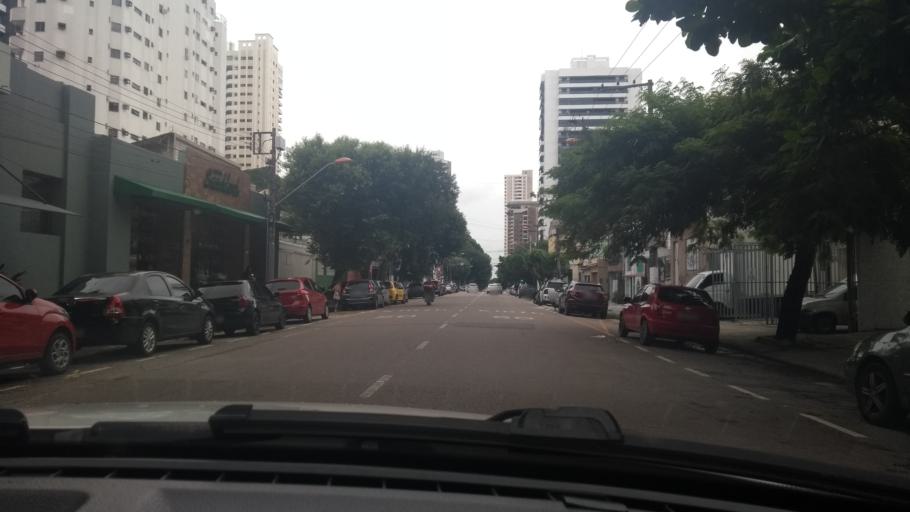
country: BR
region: Para
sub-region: Belem
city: Belem
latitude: -1.4616
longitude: -48.4917
